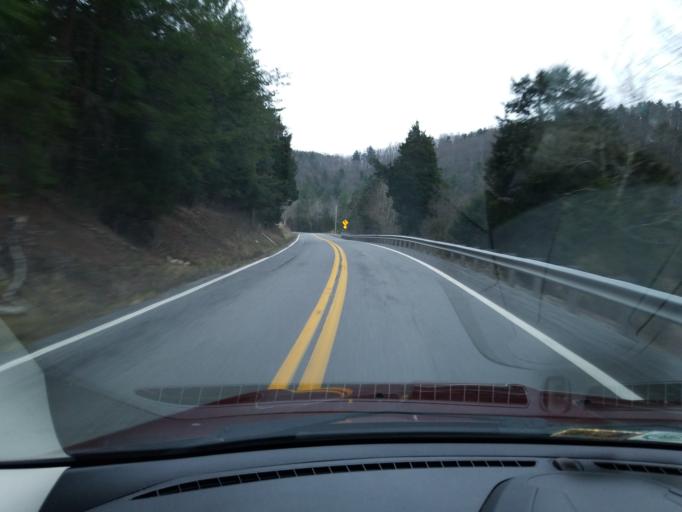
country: US
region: West Virginia
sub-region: Monroe County
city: Union
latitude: 37.5010
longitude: -80.6118
